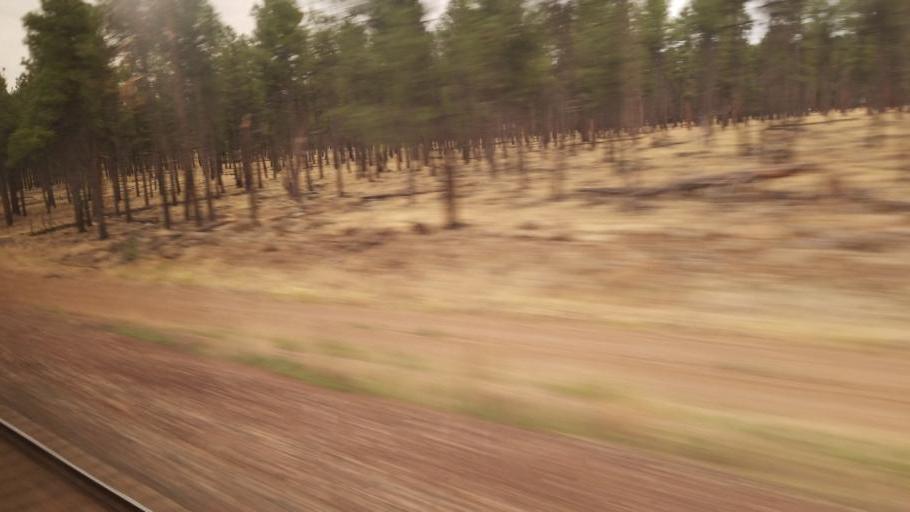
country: US
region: Arizona
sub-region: Coconino County
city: Parks
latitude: 35.2459
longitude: -112.0421
